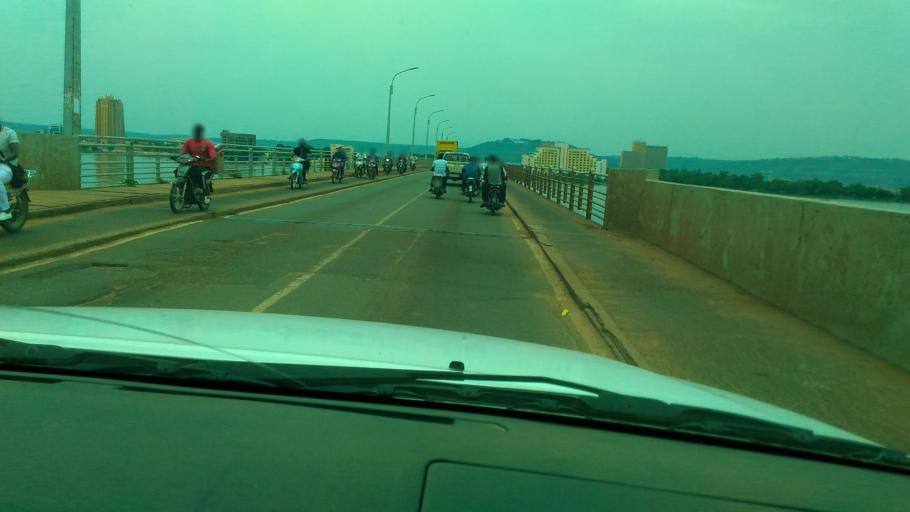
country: ML
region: Bamako
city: Bamako
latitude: 12.6269
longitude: -7.9901
